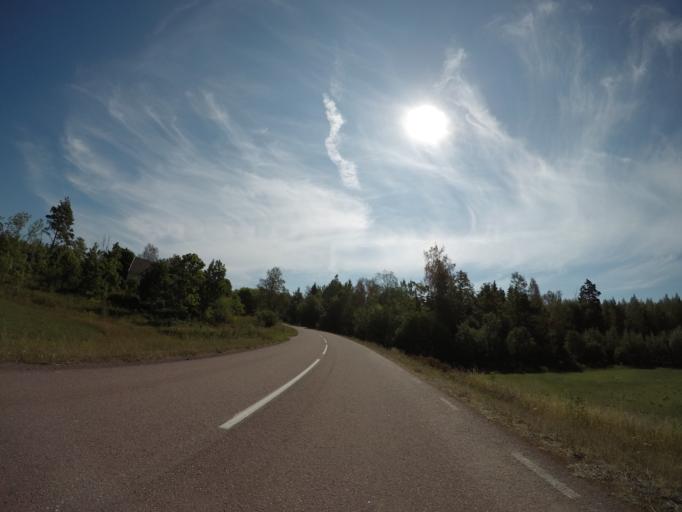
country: AX
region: Alands landsbygd
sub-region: Finstroem
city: Finstroem
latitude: 60.2751
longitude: 19.9127
